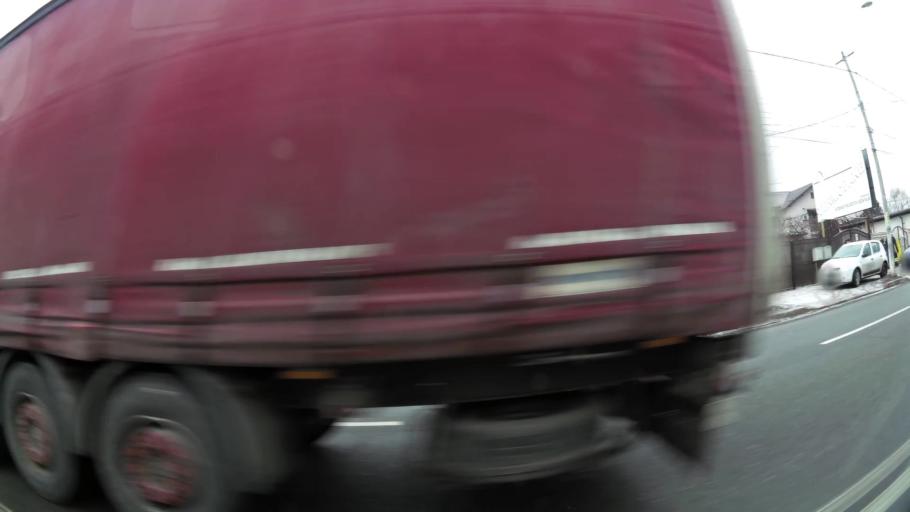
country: RO
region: Dambovita
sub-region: Comuna Ulmi
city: Ulmi
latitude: 44.9084
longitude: 25.4900
